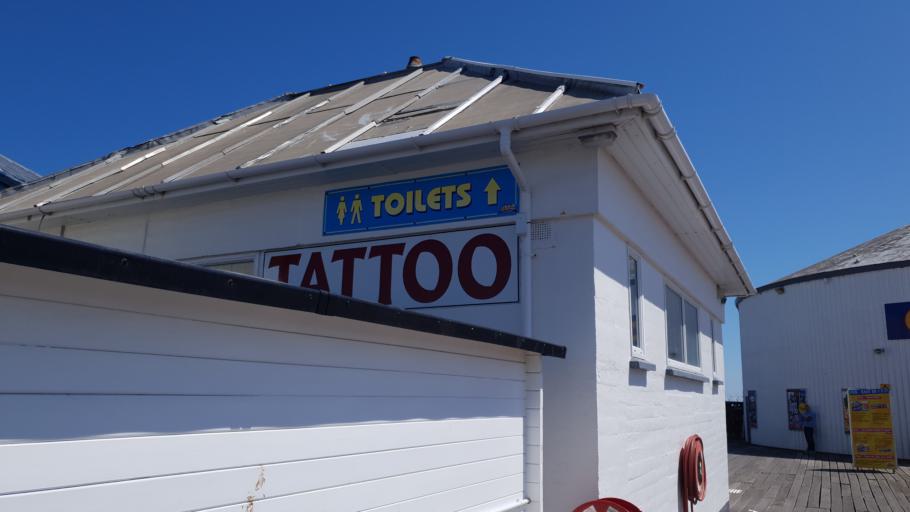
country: GB
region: England
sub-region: Essex
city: Clacton-on-Sea
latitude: 51.7849
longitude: 1.1567
